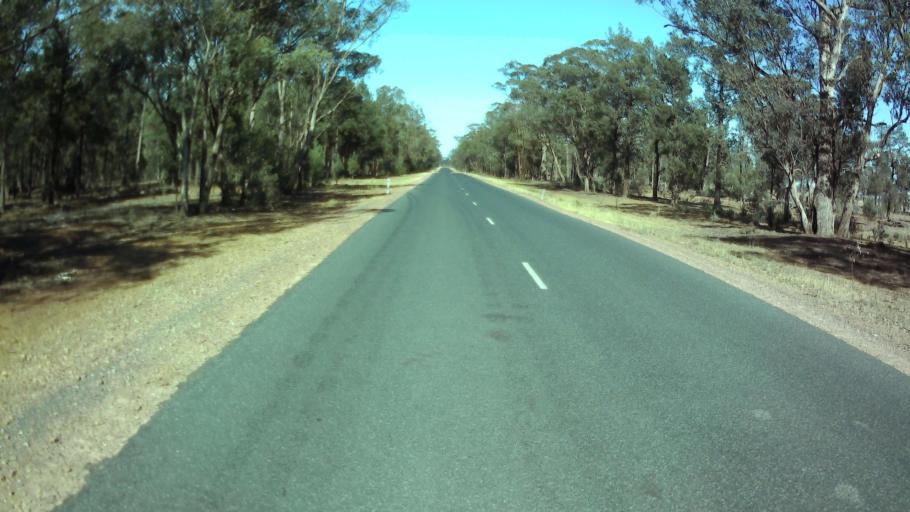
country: AU
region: New South Wales
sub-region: Weddin
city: Grenfell
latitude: -34.1130
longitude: 147.8406
